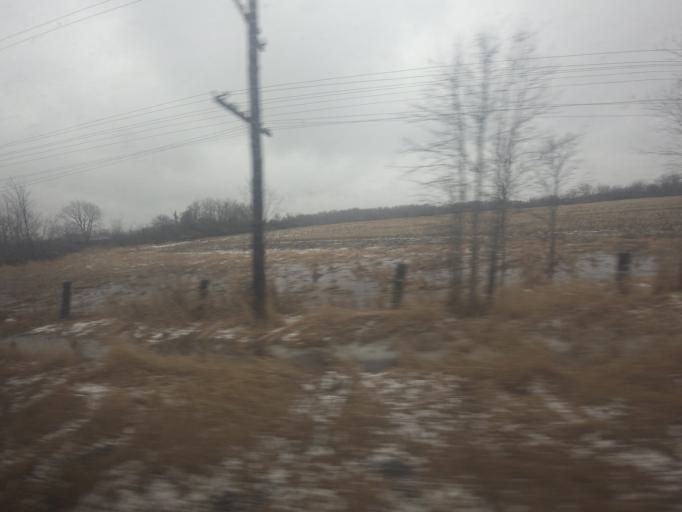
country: CA
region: Ontario
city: Deseronto
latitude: 44.2264
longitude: -77.1120
